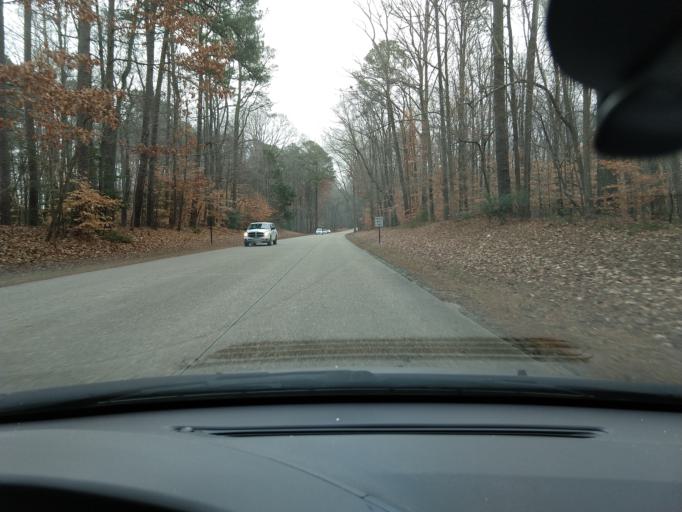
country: US
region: Virginia
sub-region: City of Williamsburg
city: Williamsburg
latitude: 37.2802
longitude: -76.6233
